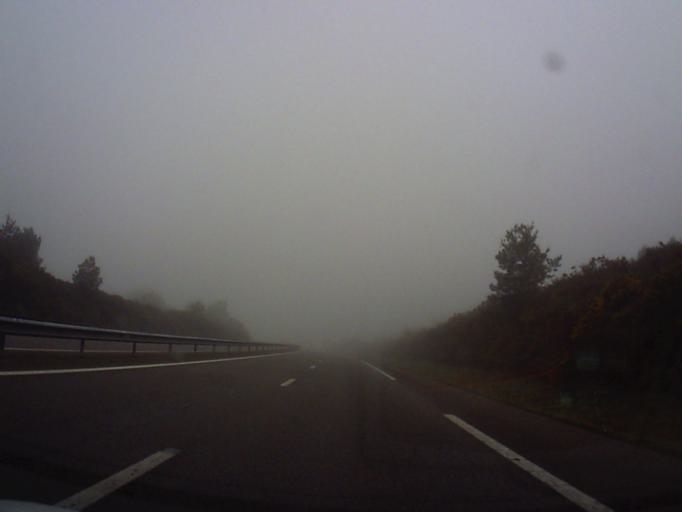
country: FR
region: Brittany
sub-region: Departement du Morbihan
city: Augan
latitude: 47.9362
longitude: -2.2552
